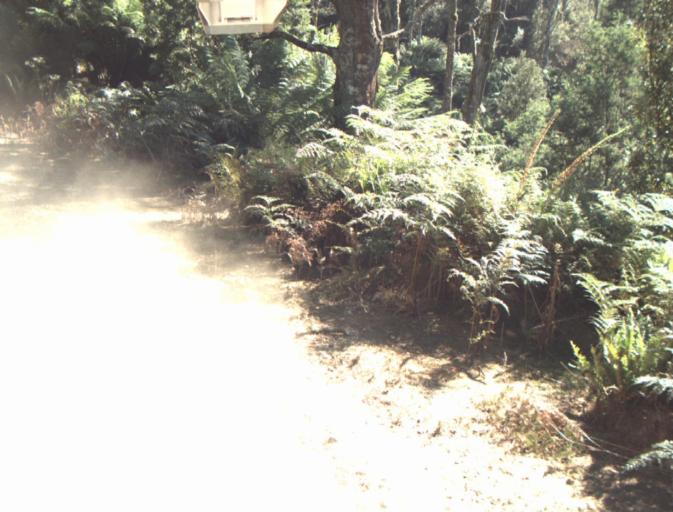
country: AU
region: Tasmania
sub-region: Dorset
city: Scottsdale
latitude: -41.2734
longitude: 147.3636
